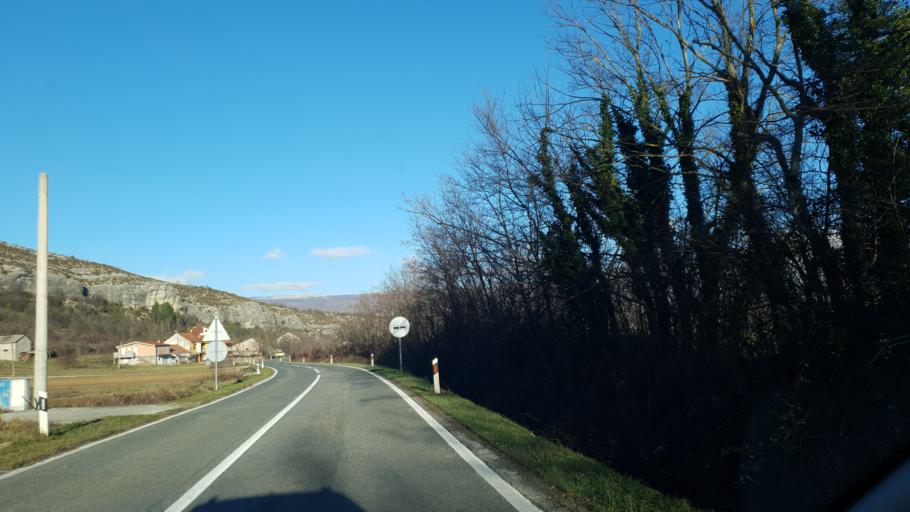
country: HR
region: Splitsko-Dalmatinska
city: Sinj
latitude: 43.7177
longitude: 16.6668
